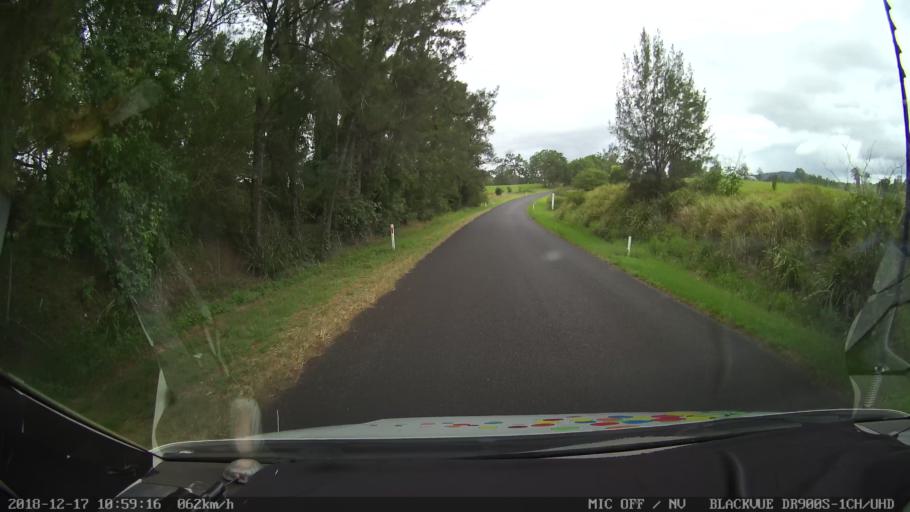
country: AU
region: New South Wales
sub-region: Richmond Valley
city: Casino
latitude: -28.8217
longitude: 152.6101
